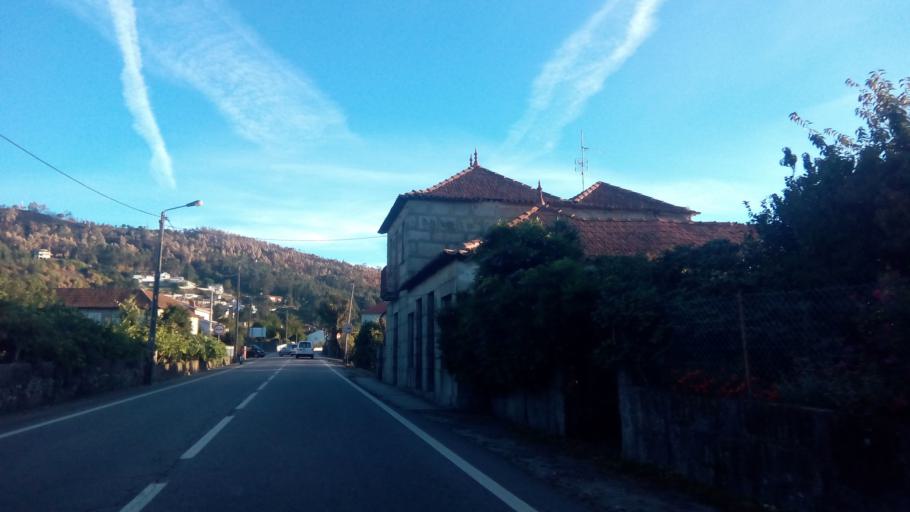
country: PT
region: Porto
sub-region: Paredes
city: Baltar
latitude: 41.1879
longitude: -8.3892
